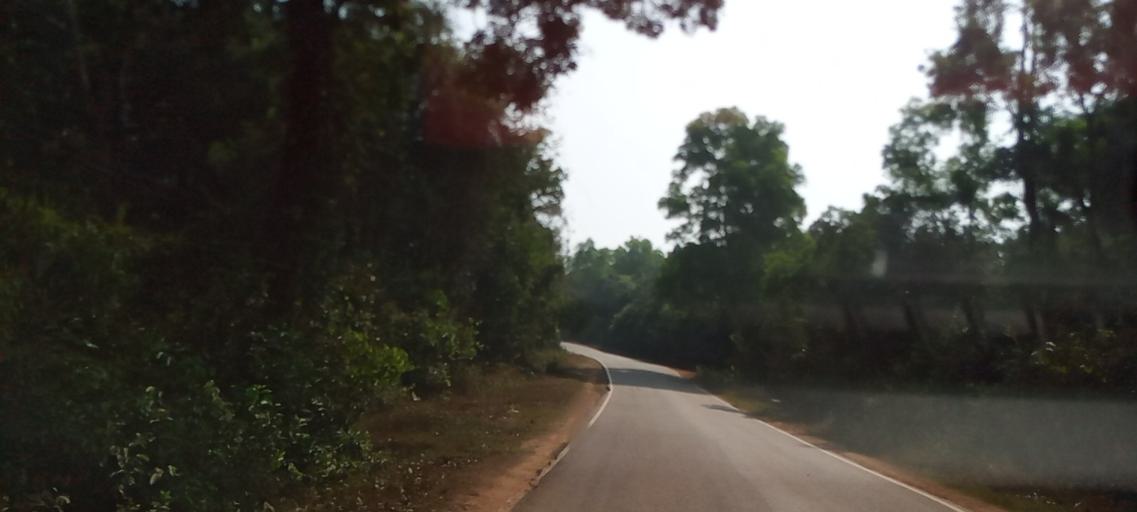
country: IN
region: Karnataka
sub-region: Udupi
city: Manipala
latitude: 13.5124
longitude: 74.8349
